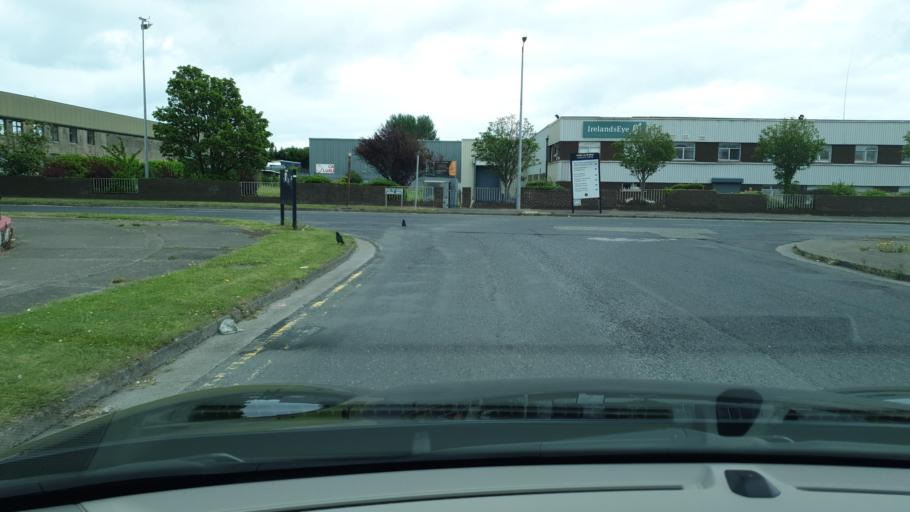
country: IE
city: Bayside
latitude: 53.3956
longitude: -6.1462
